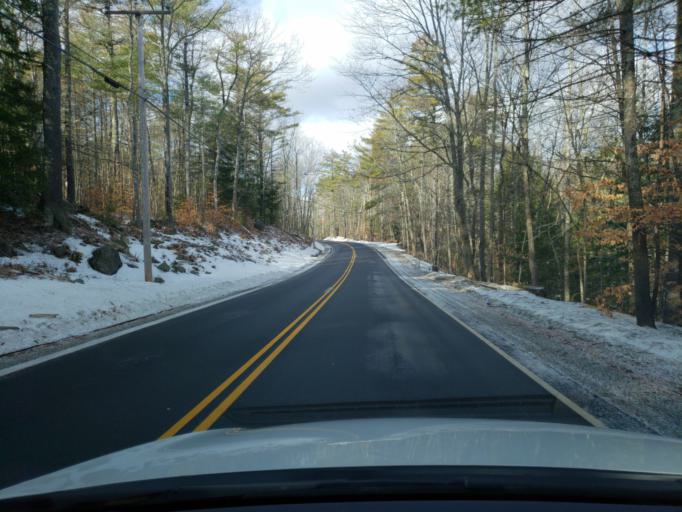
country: US
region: New Hampshire
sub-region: Hillsborough County
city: Greenfield
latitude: 42.9936
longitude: -71.8196
